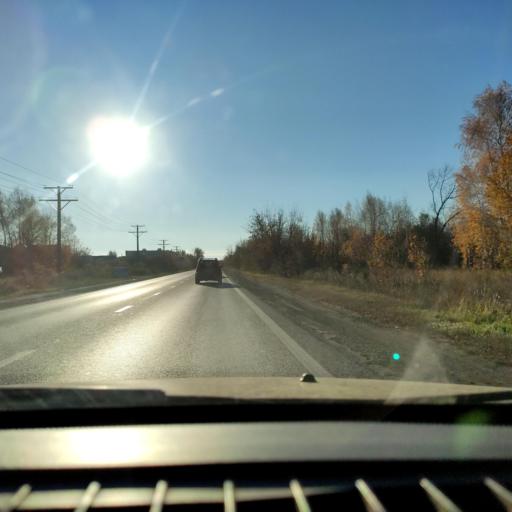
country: RU
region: Samara
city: Tol'yatti
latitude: 53.5559
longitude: 49.3649
